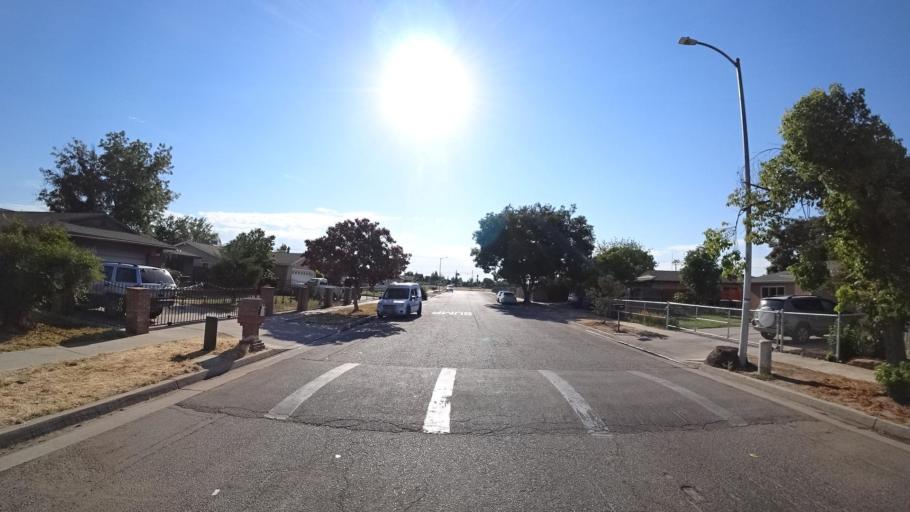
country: US
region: California
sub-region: Fresno County
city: Fresno
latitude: 36.7083
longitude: -119.7472
